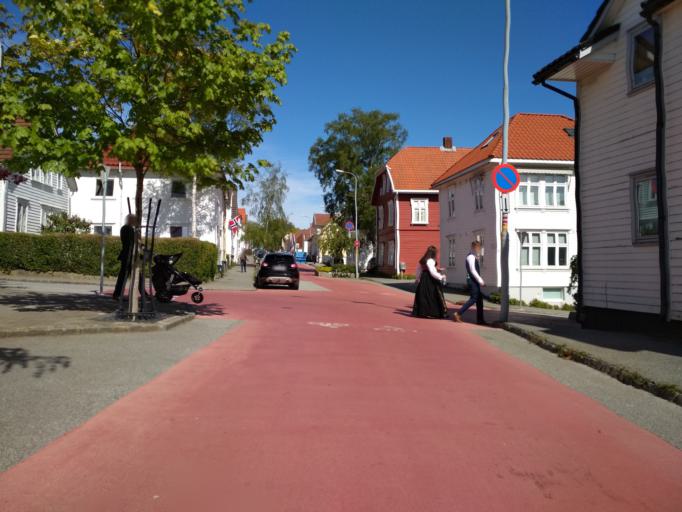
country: NO
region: Rogaland
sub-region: Stavanger
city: Stavanger
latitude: 58.9691
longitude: 5.7244
